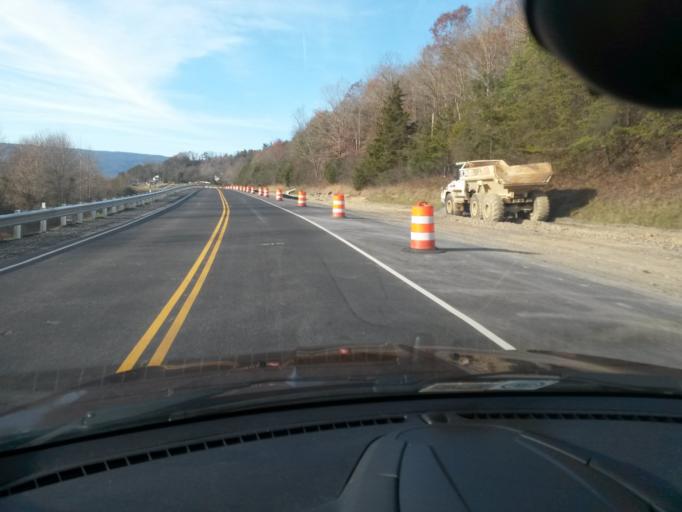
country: US
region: Virginia
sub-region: Alleghany County
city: Clifton Forge
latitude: 37.6722
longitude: -79.7966
